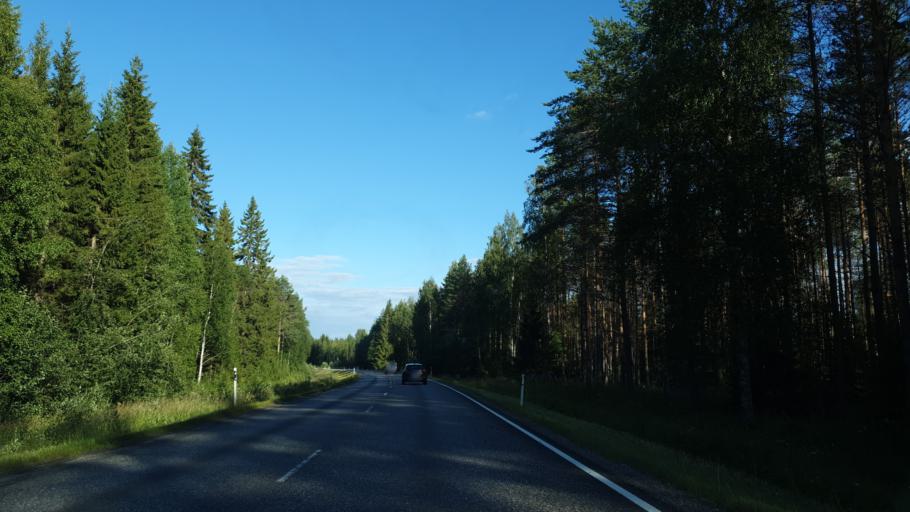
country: FI
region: North Karelia
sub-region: Joensuu
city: Outokumpu
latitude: 62.5209
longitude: 29.0078
